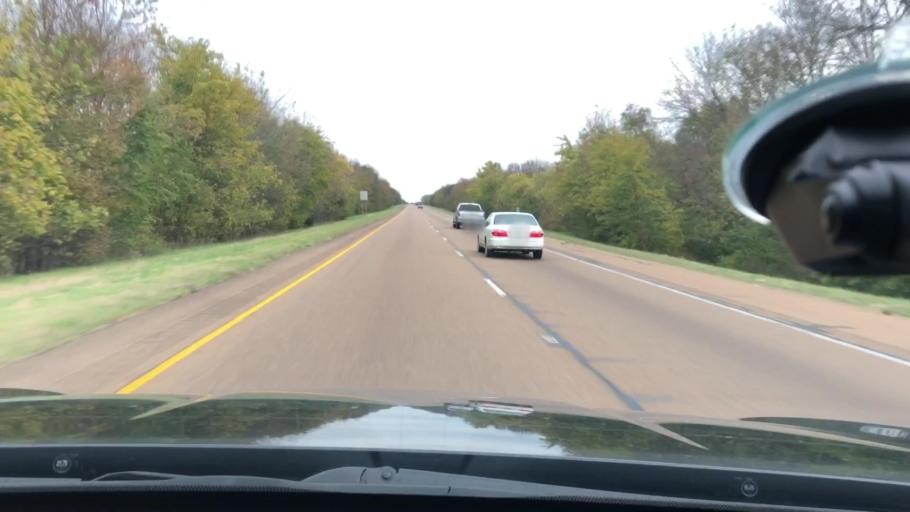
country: US
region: Arkansas
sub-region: Hempstead County
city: Hope
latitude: 33.7440
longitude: -93.5143
